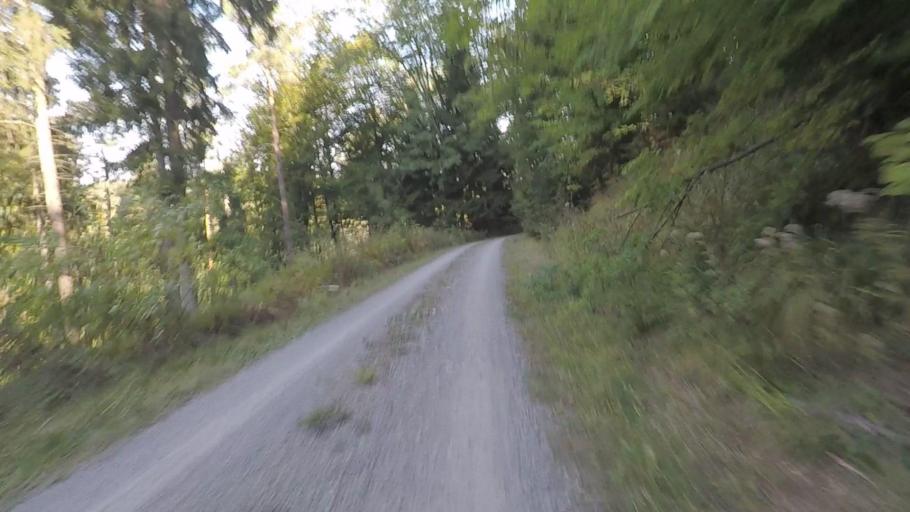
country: DE
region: Baden-Wuerttemberg
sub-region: Regierungsbezirk Stuttgart
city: Spiegelberg
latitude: 49.0518
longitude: 9.4575
